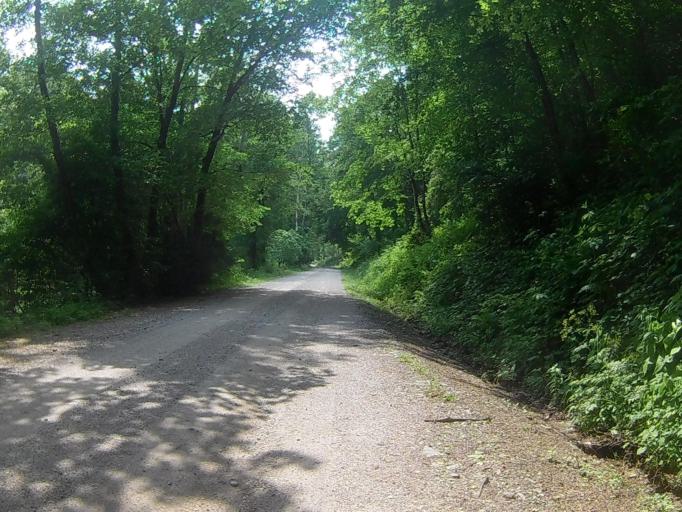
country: SI
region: Ruse
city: Bistrica ob Dravi
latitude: 46.5318
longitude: 15.5448
